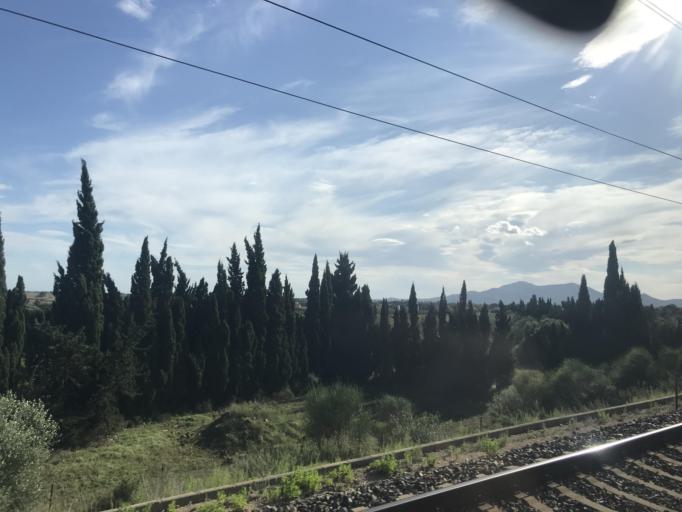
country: ES
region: Catalonia
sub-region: Provincia de Tarragona
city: Camarles
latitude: 40.7612
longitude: 0.6471
